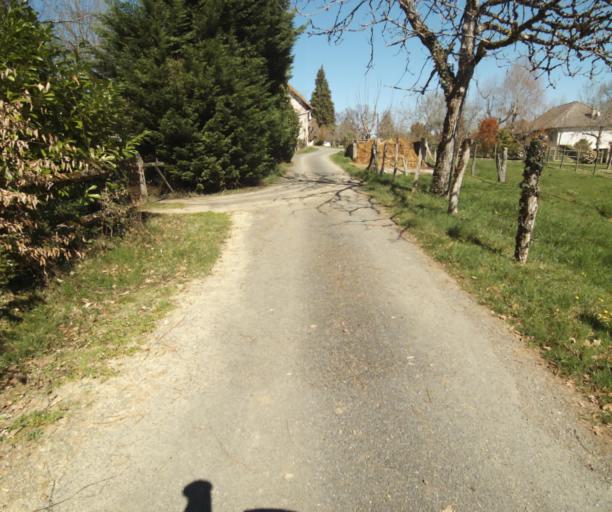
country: FR
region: Limousin
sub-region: Departement de la Correze
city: Saint-Clement
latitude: 45.3195
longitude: 1.6669
